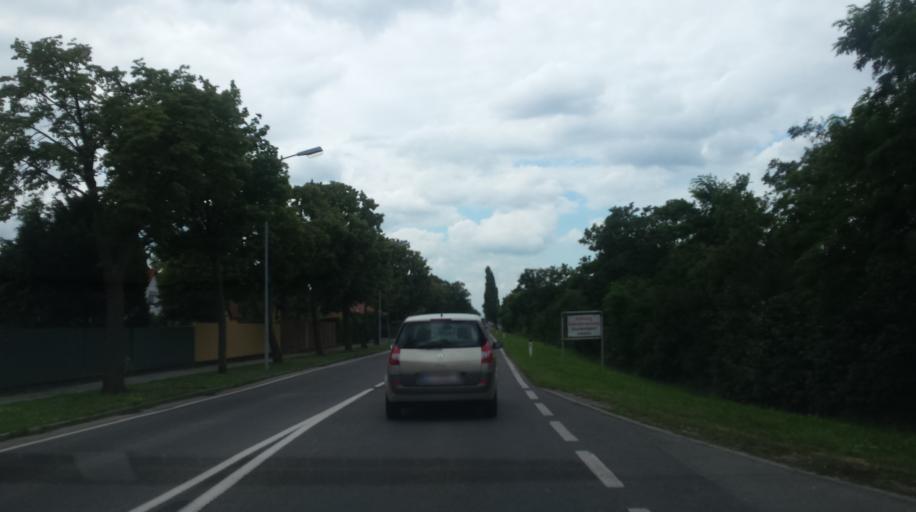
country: AT
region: Lower Austria
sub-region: Politischer Bezirk Wien-Umgebung
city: Zwolfaxing
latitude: 48.1220
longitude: 16.4585
